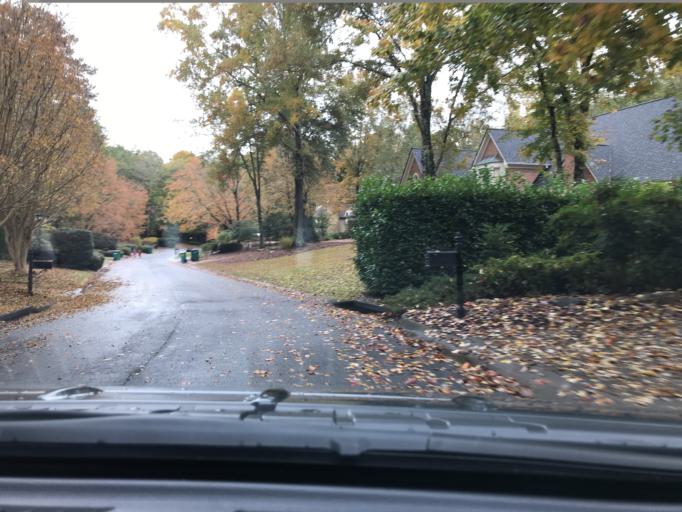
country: US
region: Georgia
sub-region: Fulton County
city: Johns Creek
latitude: 34.0040
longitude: -84.2383
